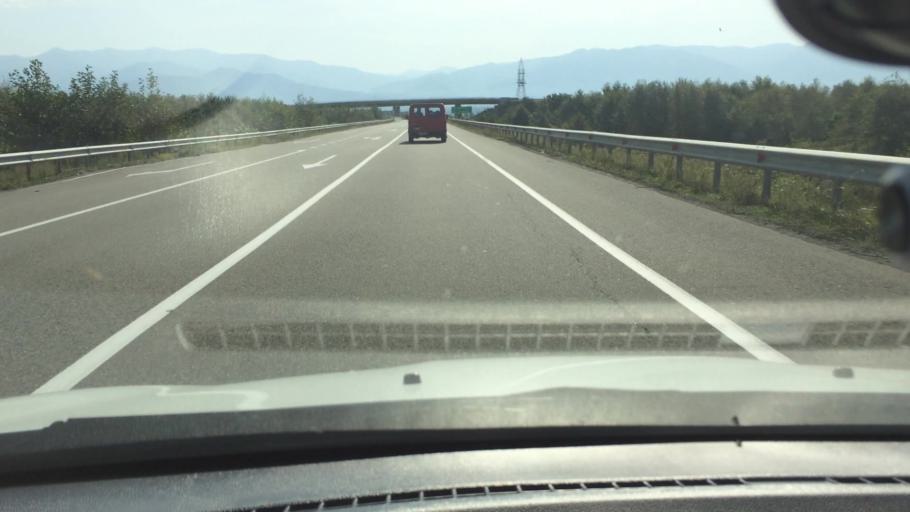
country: GE
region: Ajaria
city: Ochkhamuri
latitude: 41.8947
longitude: 41.8020
